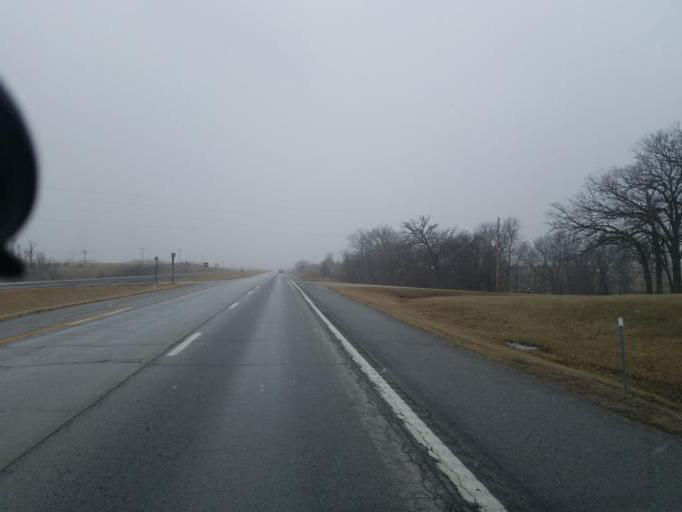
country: US
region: Missouri
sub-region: Macon County
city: La Plata
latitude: 39.9706
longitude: -92.4764
